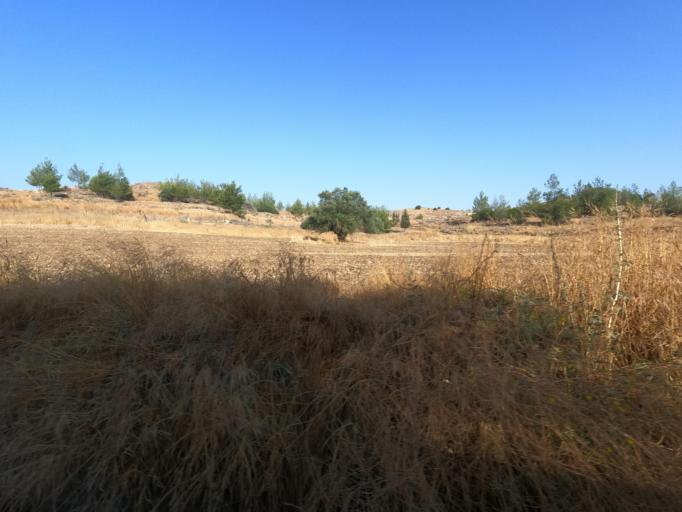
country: CY
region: Lefkosia
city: Lympia
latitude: 34.9901
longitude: 33.4373
